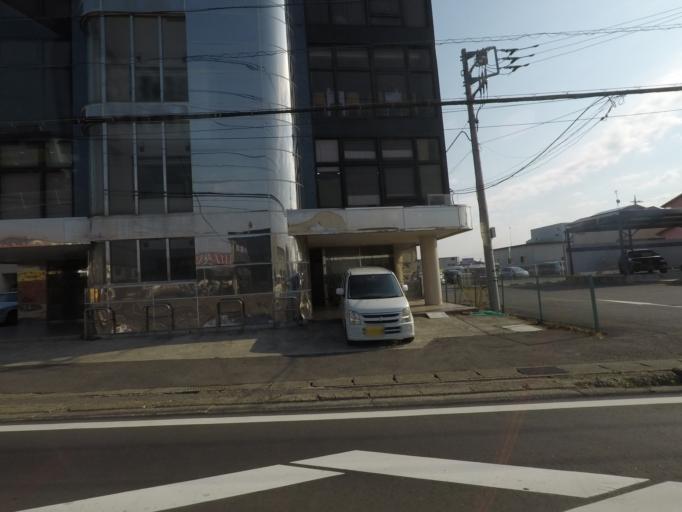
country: JP
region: Chiba
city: Narita
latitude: 35.7521
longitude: 140.3061
